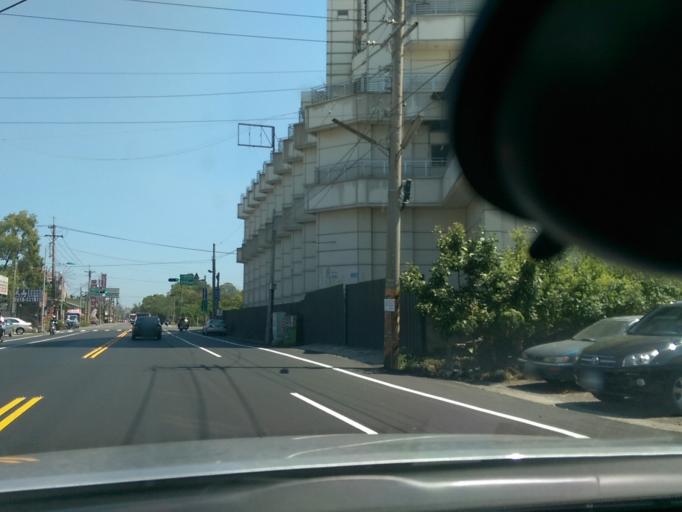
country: TW
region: Taiwan
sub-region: Chiayi
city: Jiayi Shi
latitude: 23.4388
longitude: 120.4534
